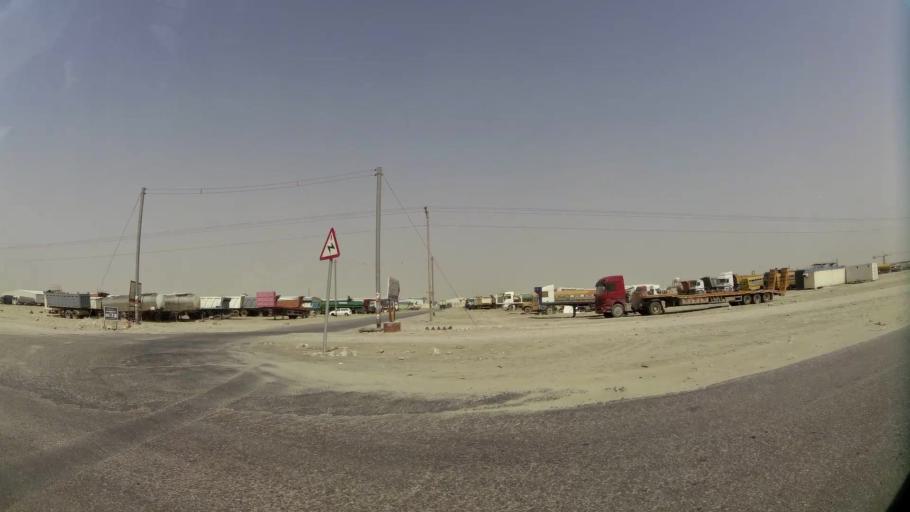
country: QA
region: Baladiyat ar Rayyan
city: Ar Rayyan
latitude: 25.2055
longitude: 51.3624
